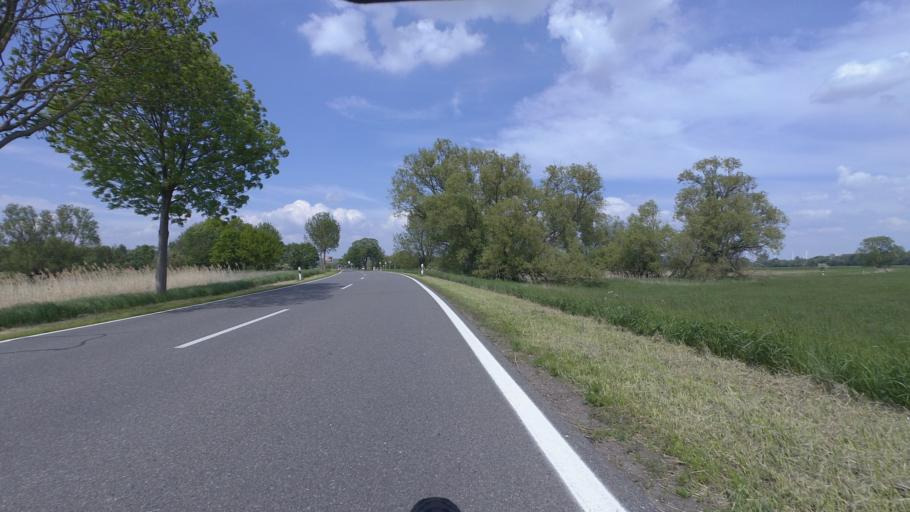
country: DE
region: Lower Saxony
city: Jerxheim
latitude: 52.0573
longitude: 10.8870
